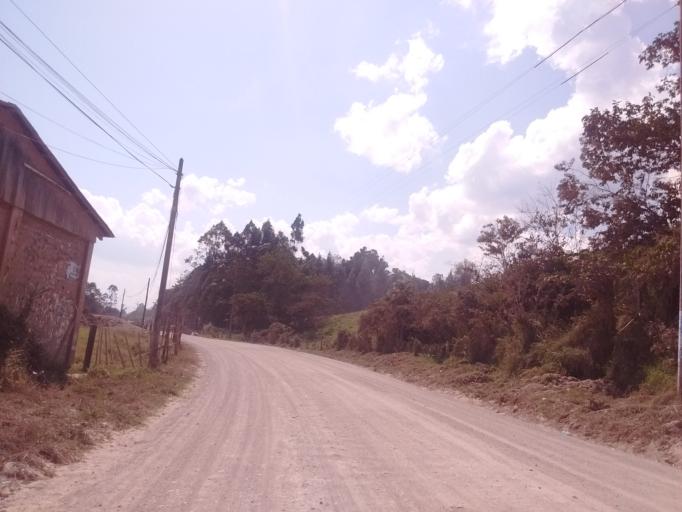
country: PE
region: Pasco
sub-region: Provincia de Oxapampa
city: Oxapampa
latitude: -10.5687
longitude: -75.4074
